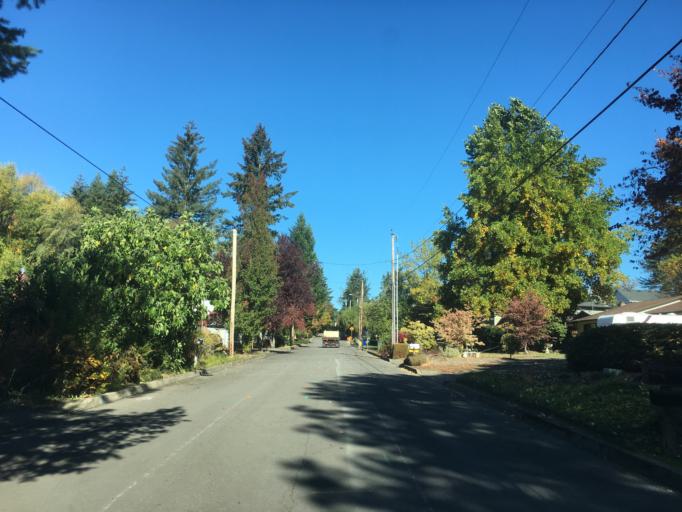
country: US
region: Oregon
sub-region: Multnomah County
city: Gresham
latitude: 45.4848
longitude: -122.4182
